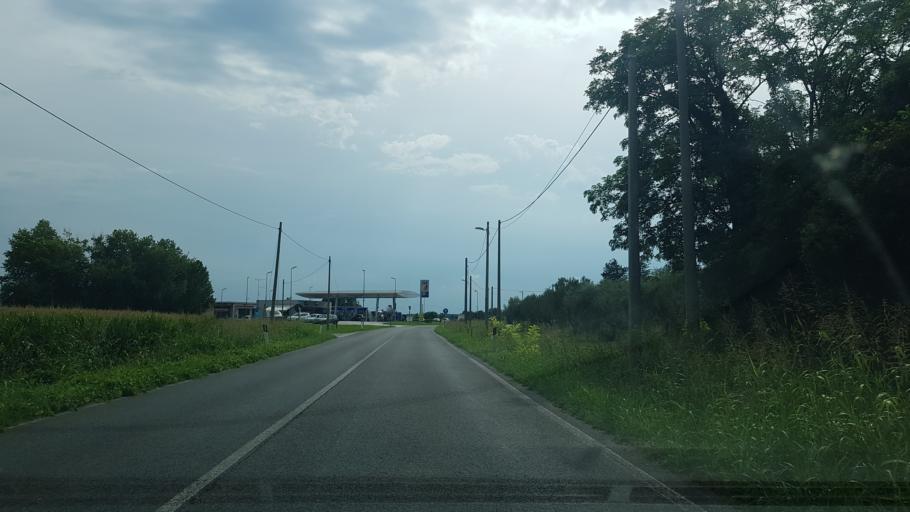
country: IT
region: Friuli Venezia Giulia
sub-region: Provincia di Gorizia
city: Staranzano
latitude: 45.8043
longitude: 13.4862
